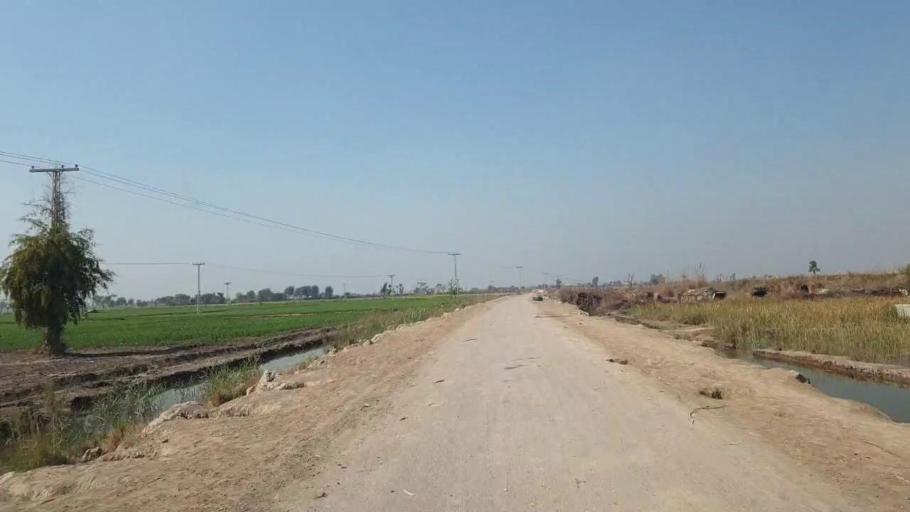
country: PK
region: Sindh
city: Bhit Shah
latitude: 25.9274
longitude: 68.4819
